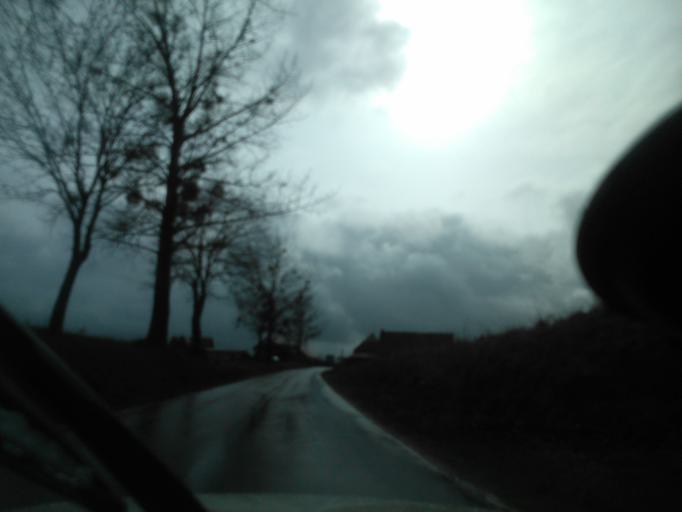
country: PL
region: Warmian-Masurian Voivodeship
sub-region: Powiat dzialdowski
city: Lidzbark
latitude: 53.3128
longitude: 19.8673
